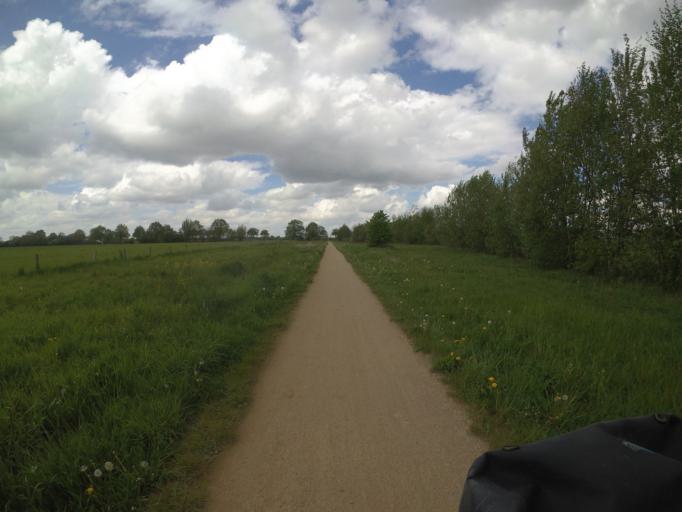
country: NL
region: North Brabant
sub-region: Gemeente Dongen
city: Dongen
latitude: 51.6261
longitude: 4.9735
